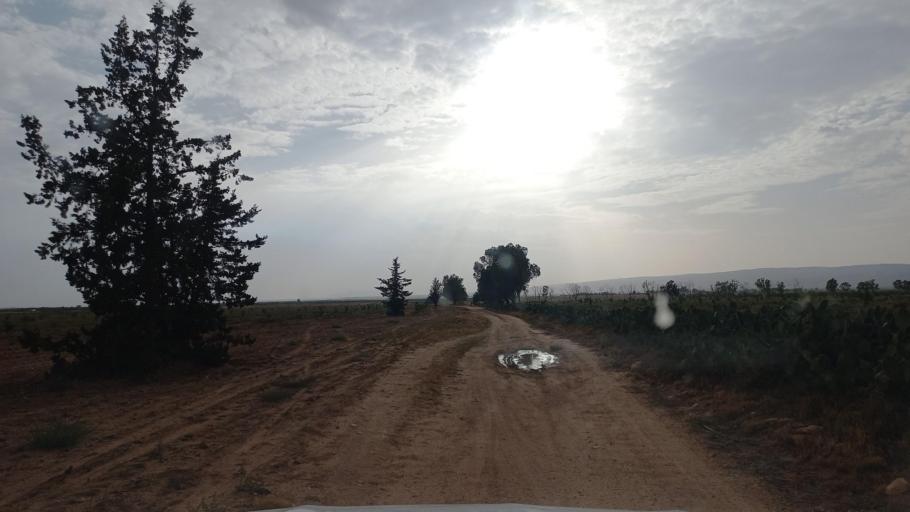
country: TN
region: Al Qasrayn
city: Sbiba
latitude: 35.2933
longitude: 9.0565
